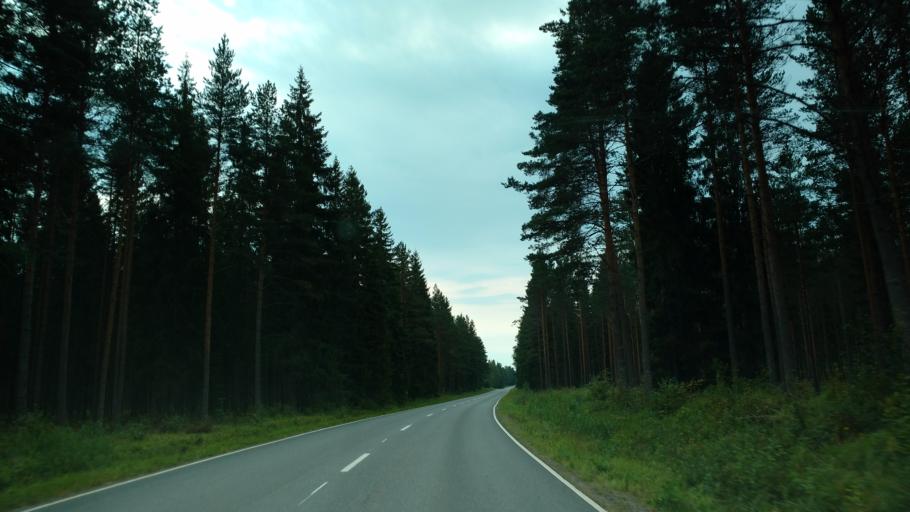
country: FI
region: Varsinais-Suomi
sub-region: Loimaa
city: Koski Tl
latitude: 60.6127
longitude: 23.1188
